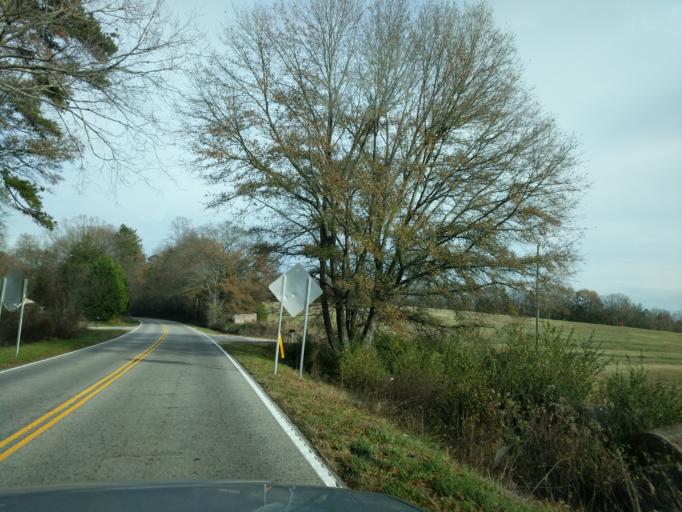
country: US
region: South Carolina
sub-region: Pickens County
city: Liberty
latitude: 34.7060
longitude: -82.6760
